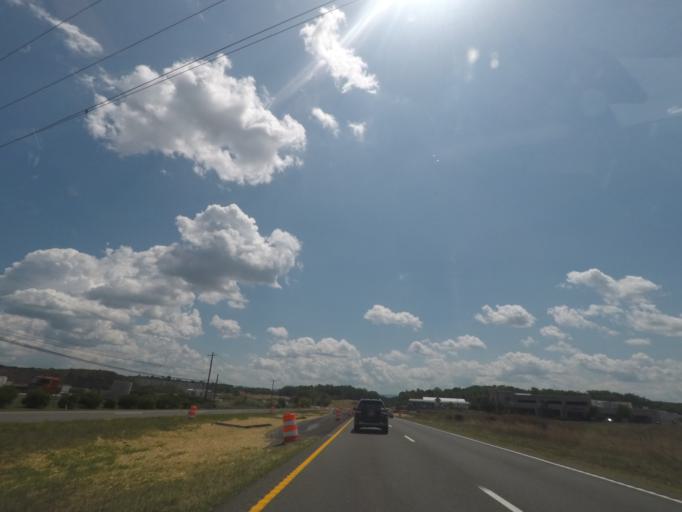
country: US
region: Virginia
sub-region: City of Winchester
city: Winchester
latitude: 39.1426
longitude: -78.1261
